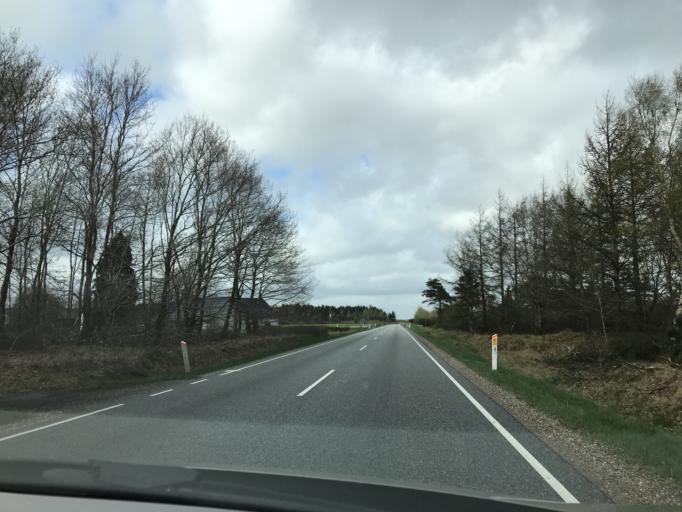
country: DK
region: Central Jutland
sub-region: Skive Kommune
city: Skive
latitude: 56.4380
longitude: 8.9637
